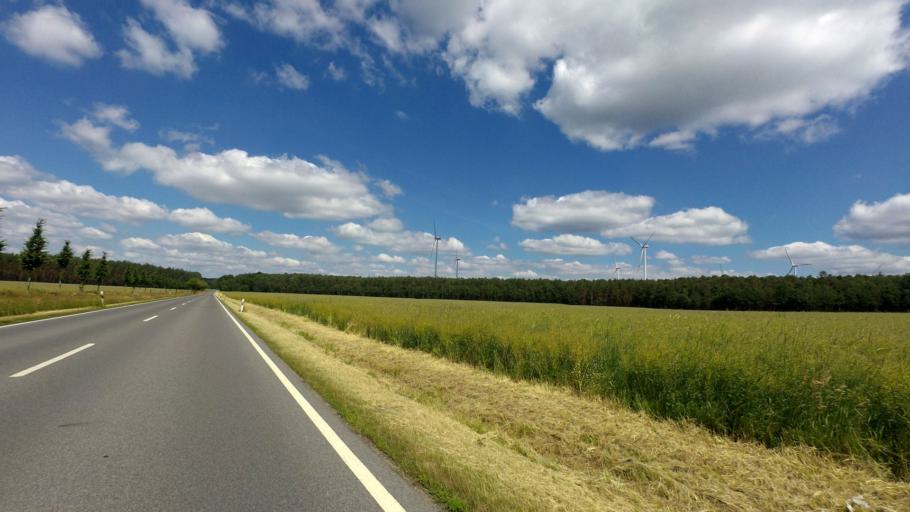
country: DE
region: Brandenburg
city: Sallgast
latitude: 51.6198
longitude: 13.7951
